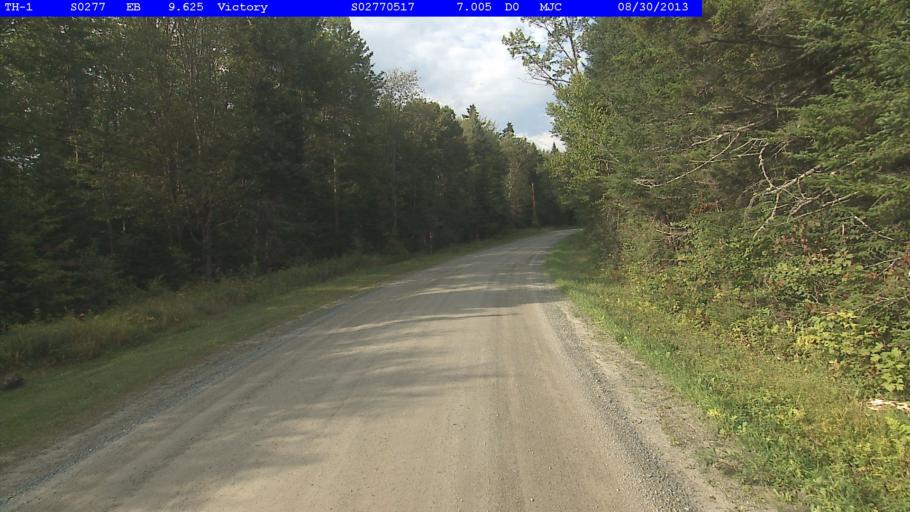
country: US
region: Vermont
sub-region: Caledonia County
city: Lyndonville
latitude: 44.5689
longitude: -71.7893
